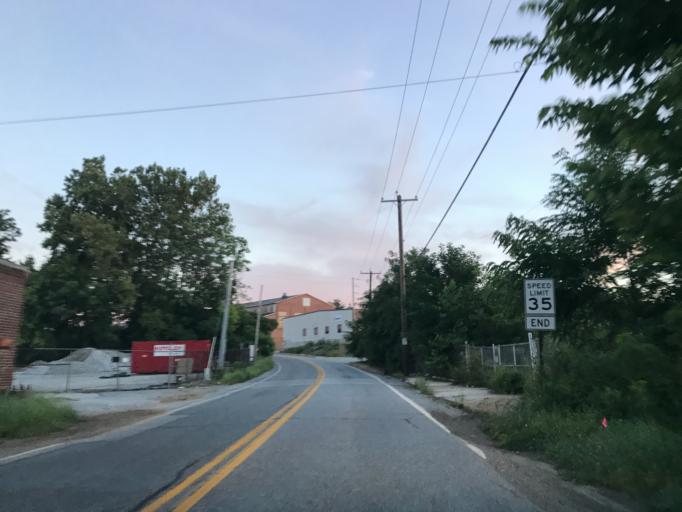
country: US
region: Pennsylvania
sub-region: York County
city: York
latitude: 39.9713
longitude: -76.7246
